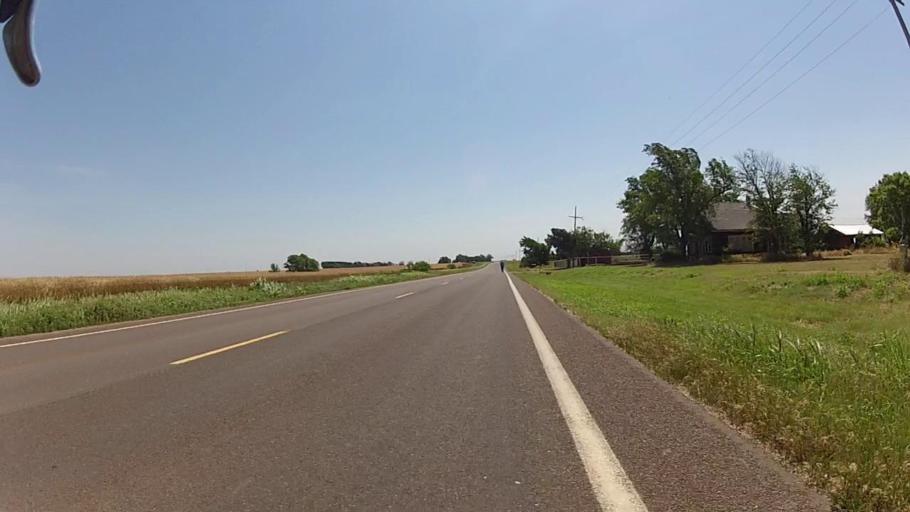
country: US
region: Kansas
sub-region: Sumner County
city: Caldwell
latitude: 37.0327
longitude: -97.5716
